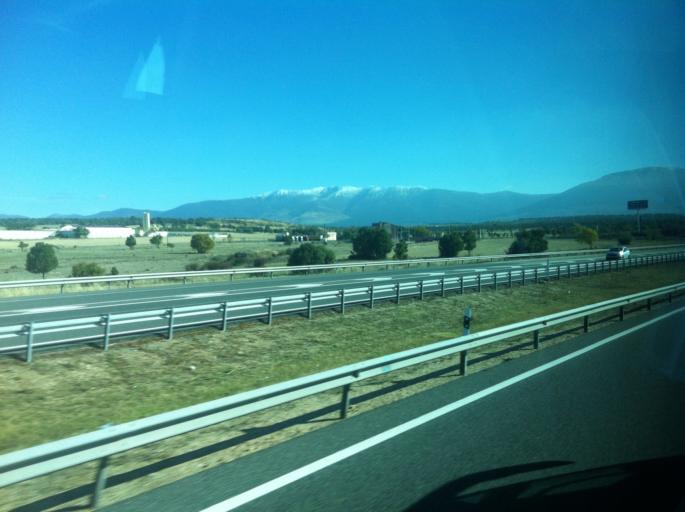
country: ES
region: Castille and Leon
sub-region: Provincia de Segovia
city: Castillejo de Mesleon
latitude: 41.2621
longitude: -3.5948
